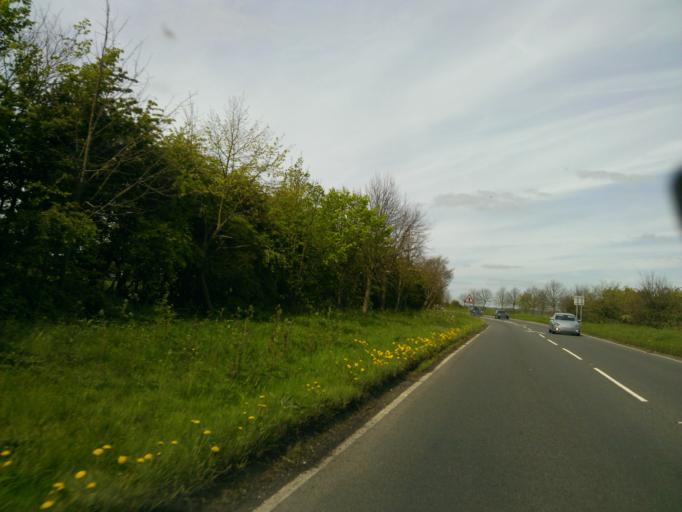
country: GB
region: England
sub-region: Essex
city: Earls Colne
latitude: 51.9320
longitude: 0.6632
